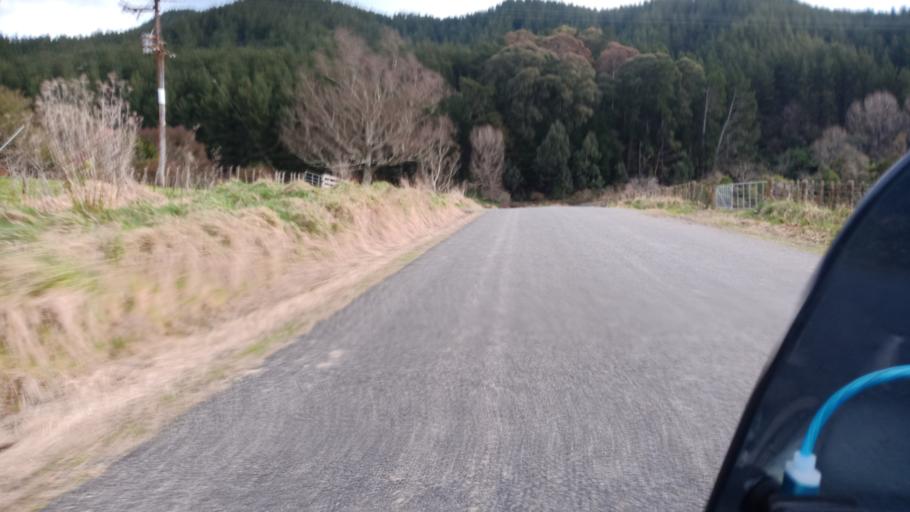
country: NZ
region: Hawke's Bay
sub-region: Wairoa District
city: Wairoa
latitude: -38.8183
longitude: 177.4743
